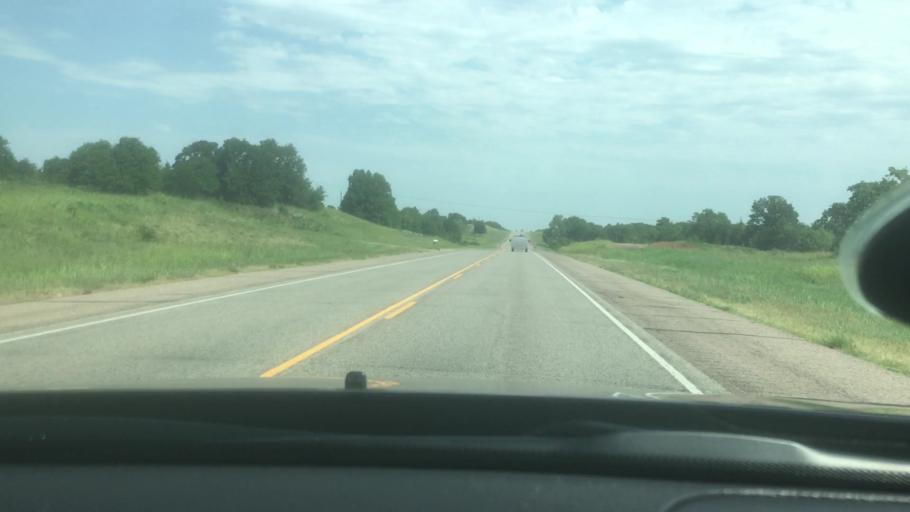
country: US
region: Oklahoma
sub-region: Seminole County
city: Konawa
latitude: 35.0209
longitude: -96.9314
